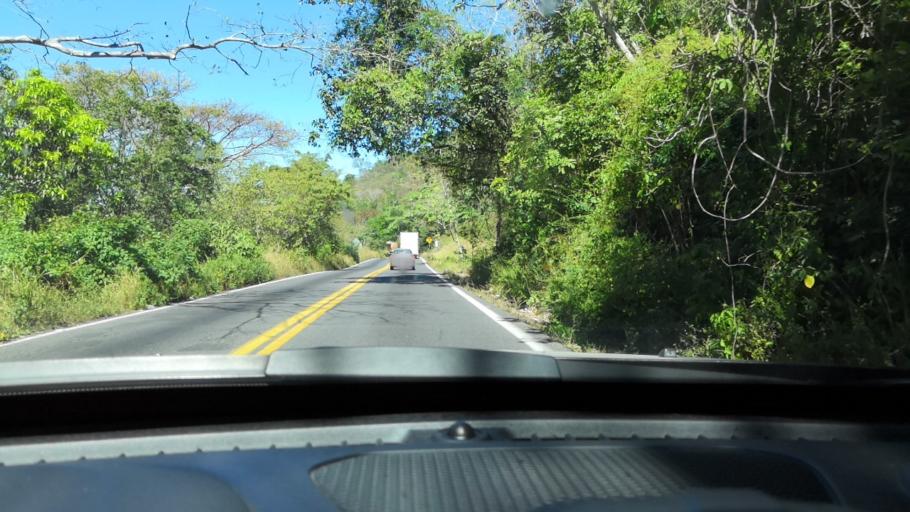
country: MX
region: Nayarit
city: Compostela
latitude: 21.2127
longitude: -104.9912
